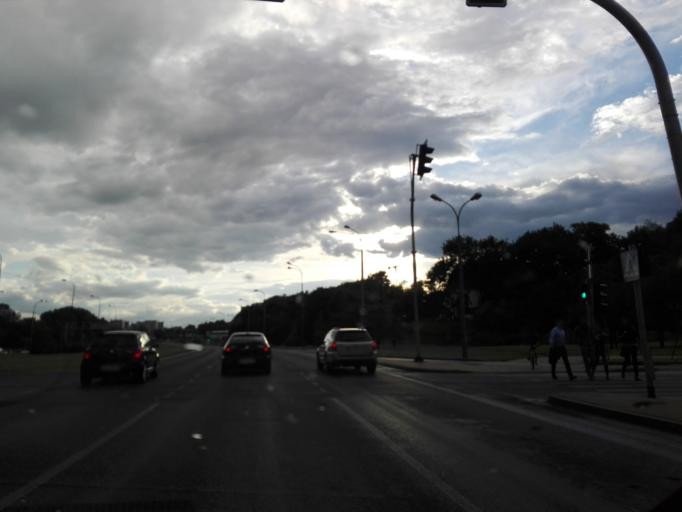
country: PL
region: Lublin Voivodeship
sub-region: Powiat lubelski
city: Lublin
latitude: 51.2533
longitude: 22.5613
